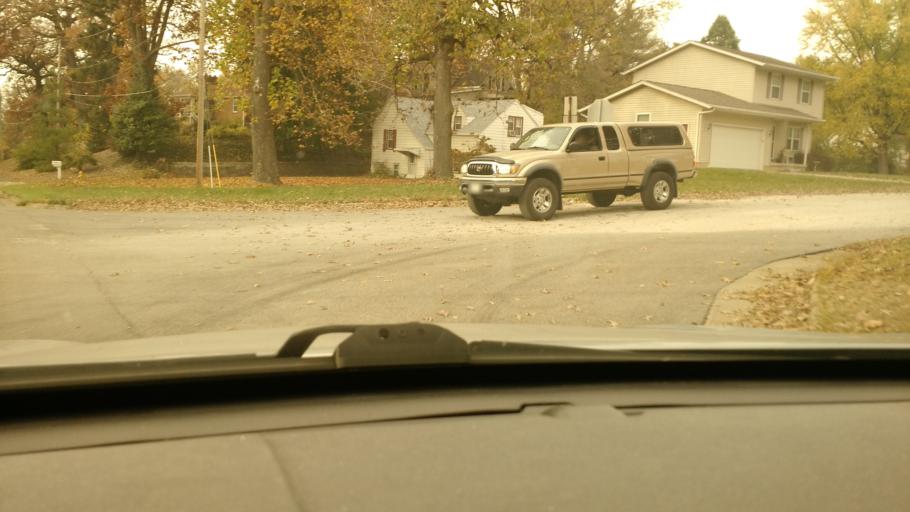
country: US
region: Illinois
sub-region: Rock Island County
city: Milan
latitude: 41.4655
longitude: -90.5772
